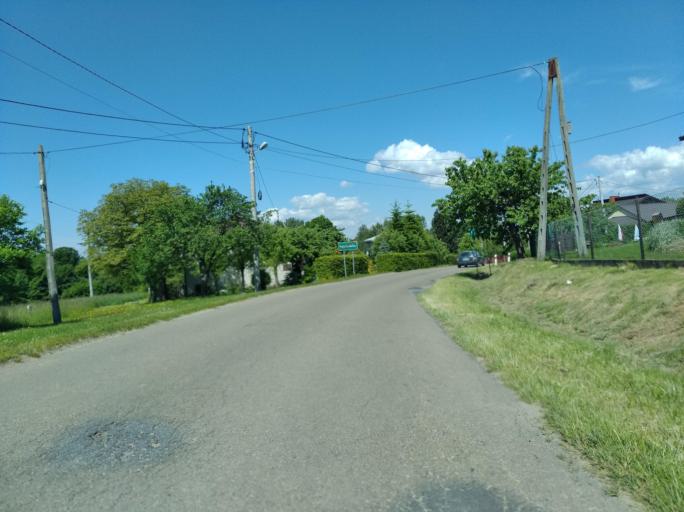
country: PL
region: Subcarpathian Voivodeship
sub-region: Powiat jasielski
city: Tarnowiec
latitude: 49.7221
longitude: 21.5949
